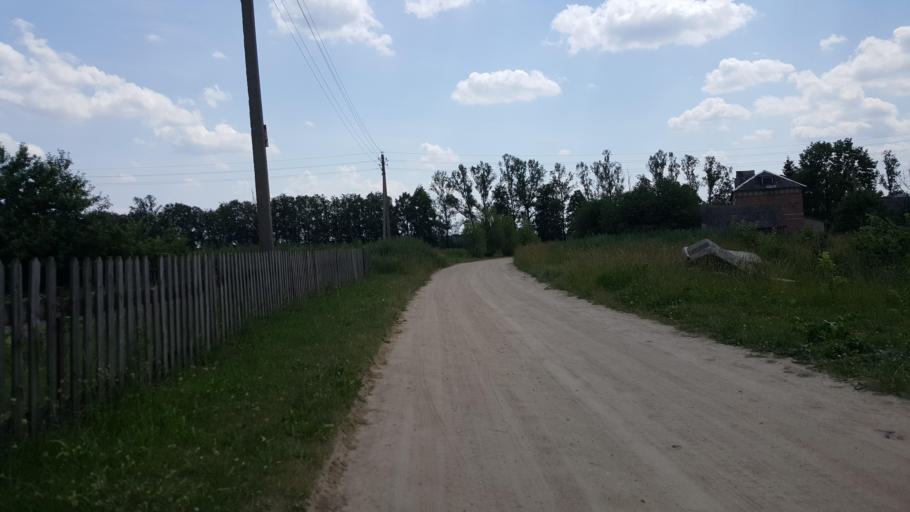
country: BY
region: Brest
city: Kamyanyets
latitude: 52.3960
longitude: 23.7650
